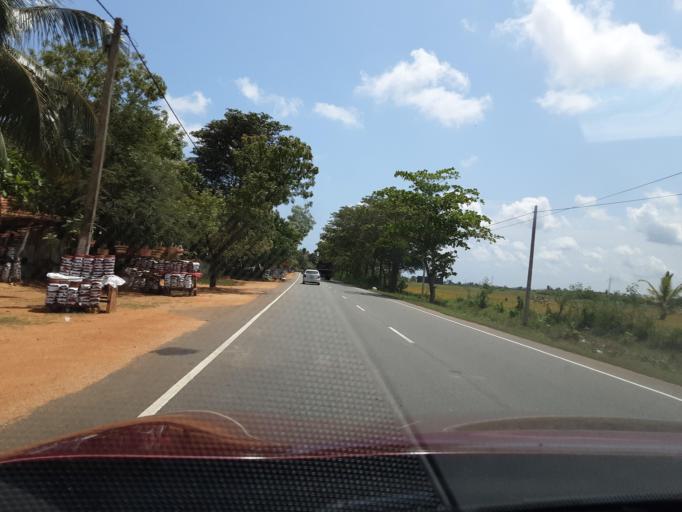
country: LK
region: Southern
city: Tangalla
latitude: 6.2228
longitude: 81.2186
